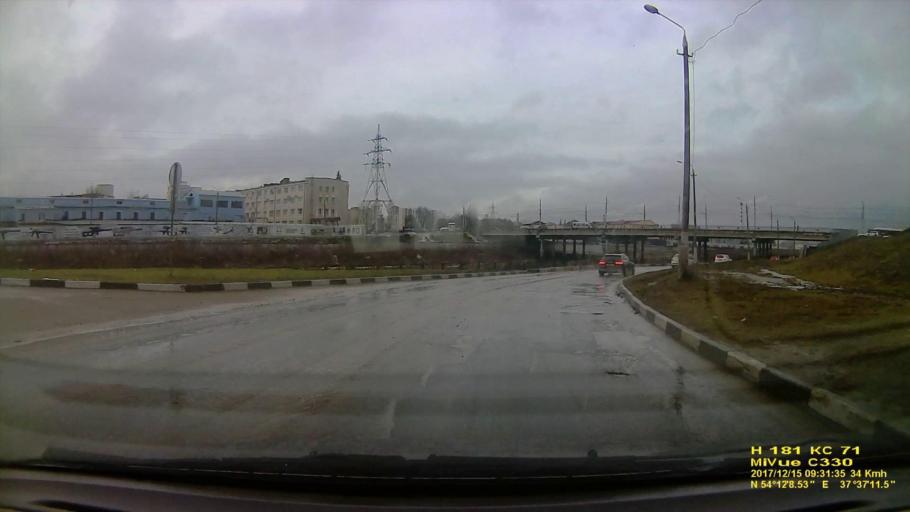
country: RU
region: Tula
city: Tula
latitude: 54.2023
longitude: 37.6200
